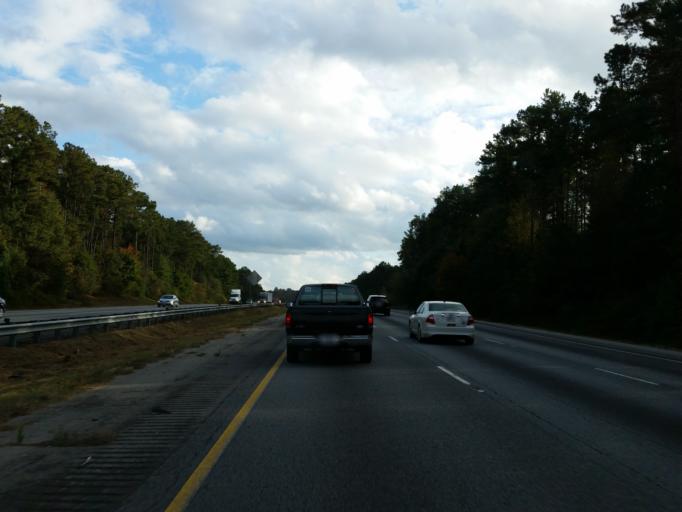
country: US
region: Georgia
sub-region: Henry County
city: Locust Grove
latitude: 33.2853
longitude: -84.1088
